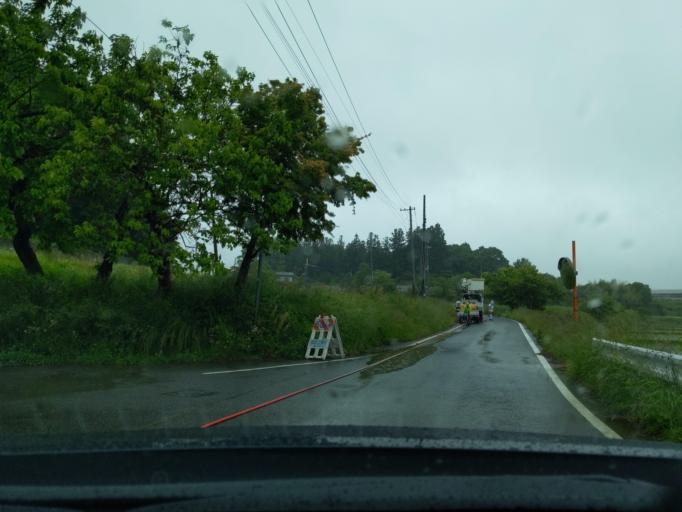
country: JP
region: Fukushima
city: Yanagawamachi-saiwaicho
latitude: 37.6538
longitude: 140.7273
